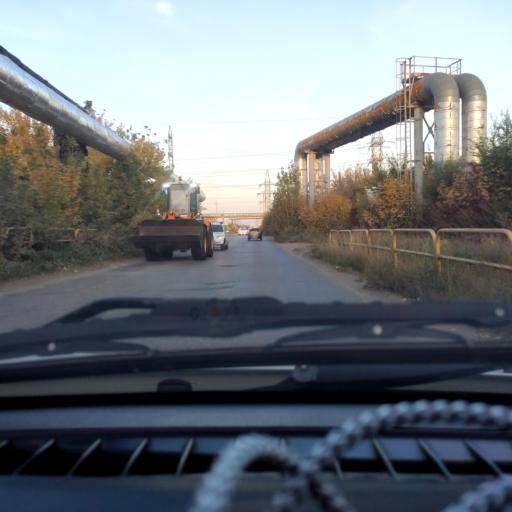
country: RU
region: Samara
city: Tol'yatti
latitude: 53.5445
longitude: 49.4447
